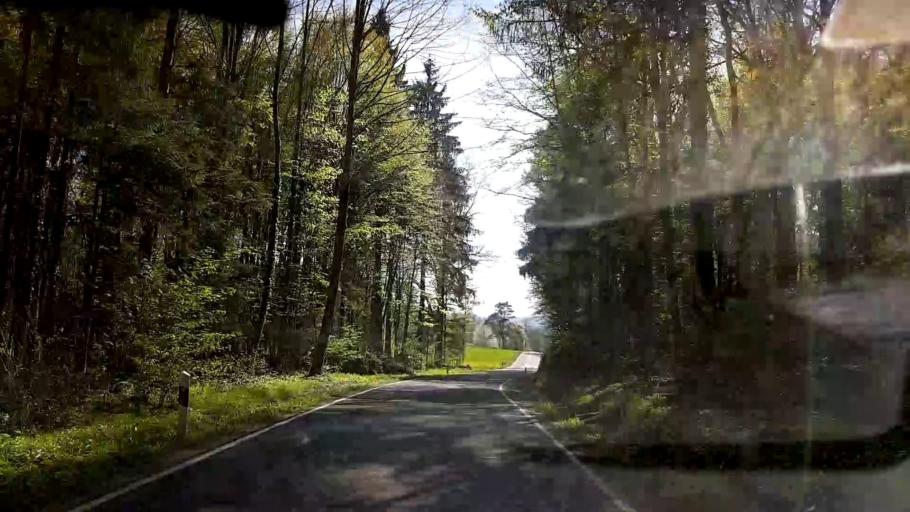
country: DE
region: Bavaria
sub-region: Upper Franconia
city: Pottenstein
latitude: 49.7960
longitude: 11.3975
